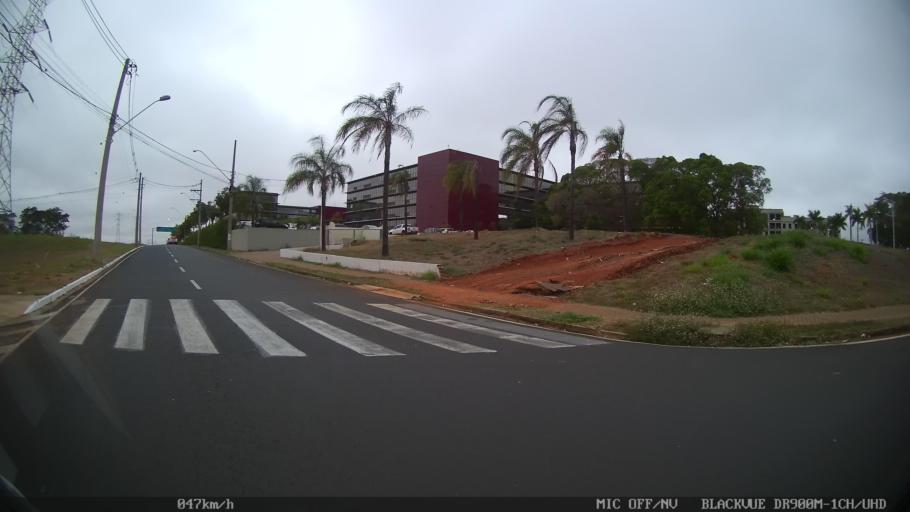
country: BR
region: Sao Paulo
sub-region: Sao Jose Do Rio Preto
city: Sao Jose do Rio Preto
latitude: -20.8450
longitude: -49.4027
